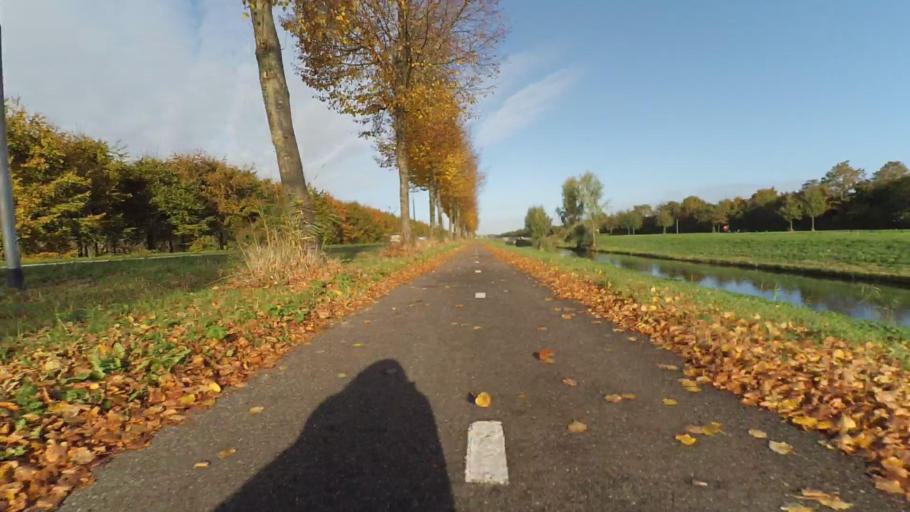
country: NL
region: Flevoland
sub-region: Gemeente Zeewolde
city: Zeewolde
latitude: 52.3340
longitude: 5.5127
